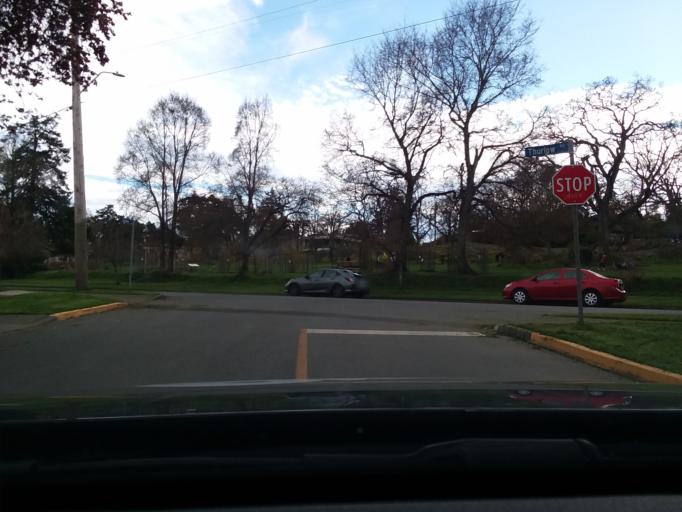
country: CA
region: British Columbia
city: Victoria
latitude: 48.4154
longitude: -123.3456
